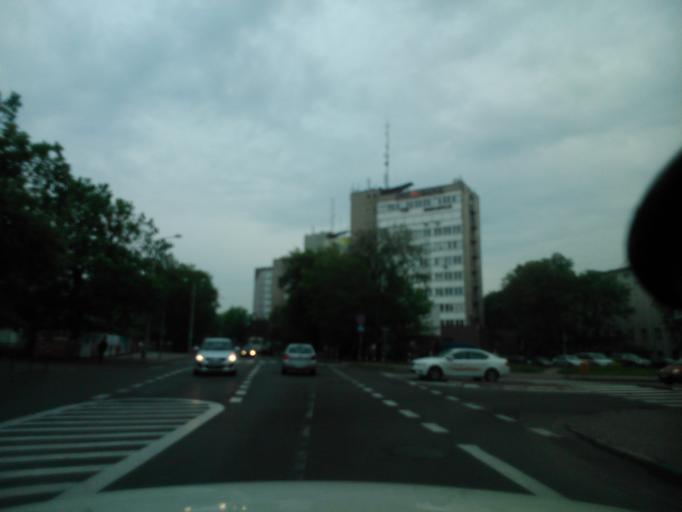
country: PL
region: Kujawsko-Pomorskie
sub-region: Torun
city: Torun
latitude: 53.0161
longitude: 18.6020
